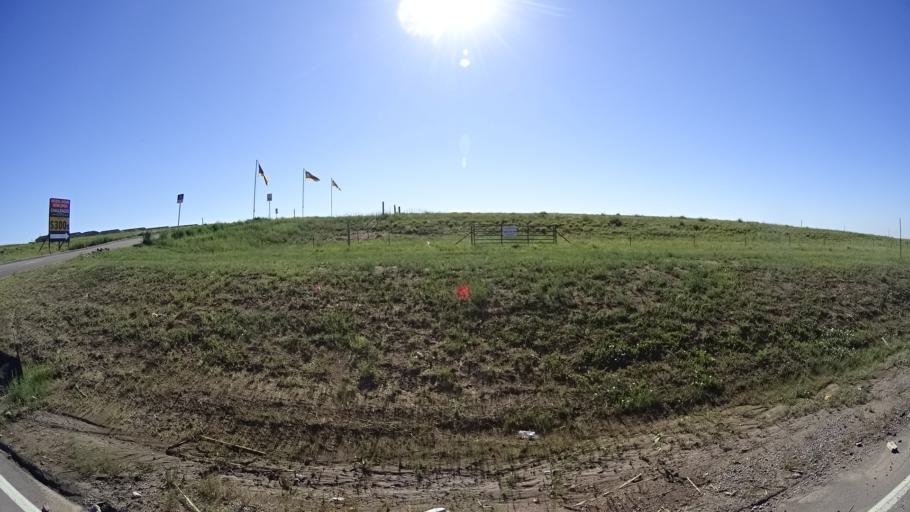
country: US
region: Colorado
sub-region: El Paso County
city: Cimarron Hills
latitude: 38.8934
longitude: -104.6827
